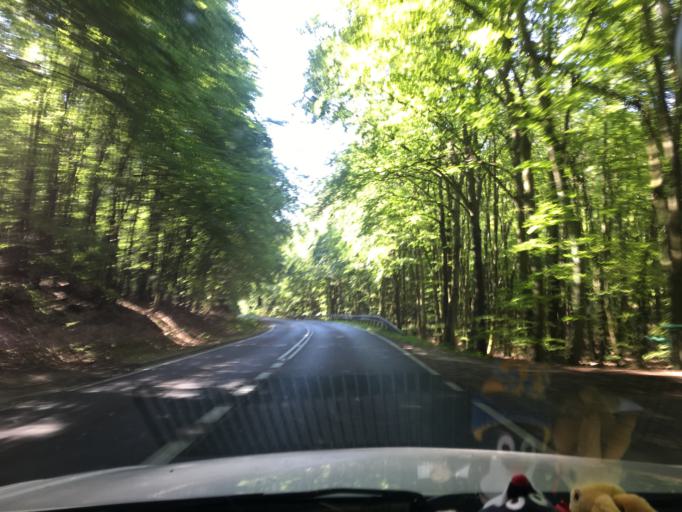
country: PL
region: West Pomeranian Voivodeship
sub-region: Powiat kamienski
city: Miedzyzdroje
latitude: 53.9511
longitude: 14.4918
